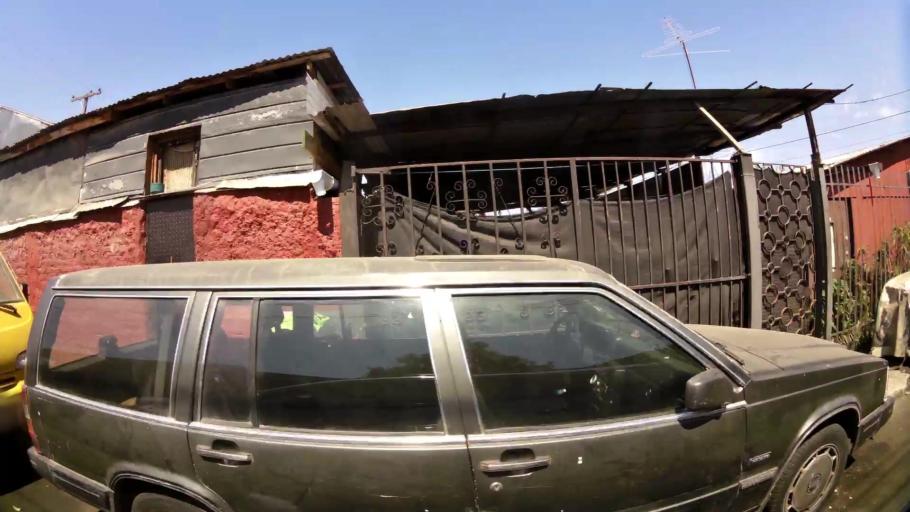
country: CL
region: Santiago Metropolitan
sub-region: Provincia de Talagante
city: Talagante
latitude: -33.6585
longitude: -70.9221
